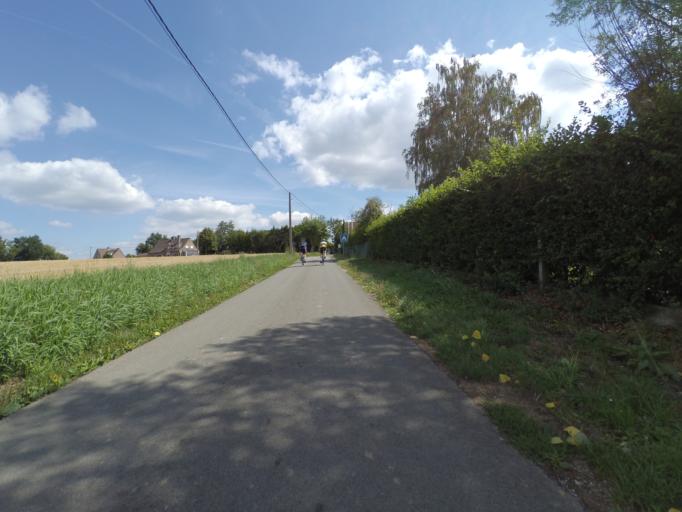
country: BE
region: Wallonia
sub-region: Province du Hainaut
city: Ellezelles
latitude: 50.7989
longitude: 3.6910
